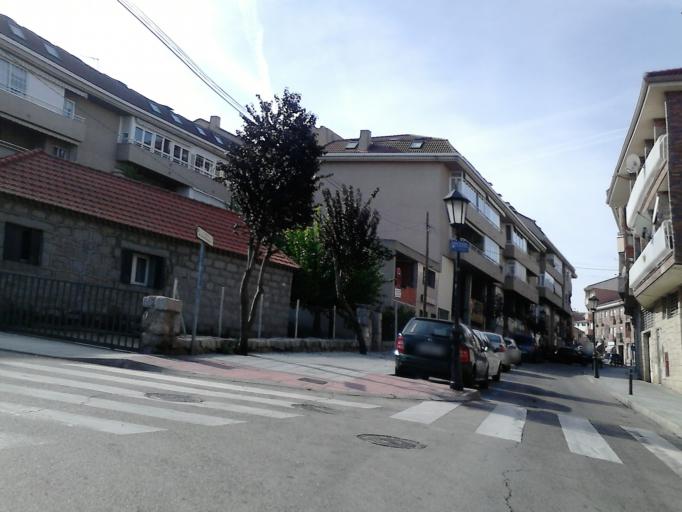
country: ES
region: Madrid
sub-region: Provincia de Madrid
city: Galapagar
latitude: 40.5803
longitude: -4.0020
